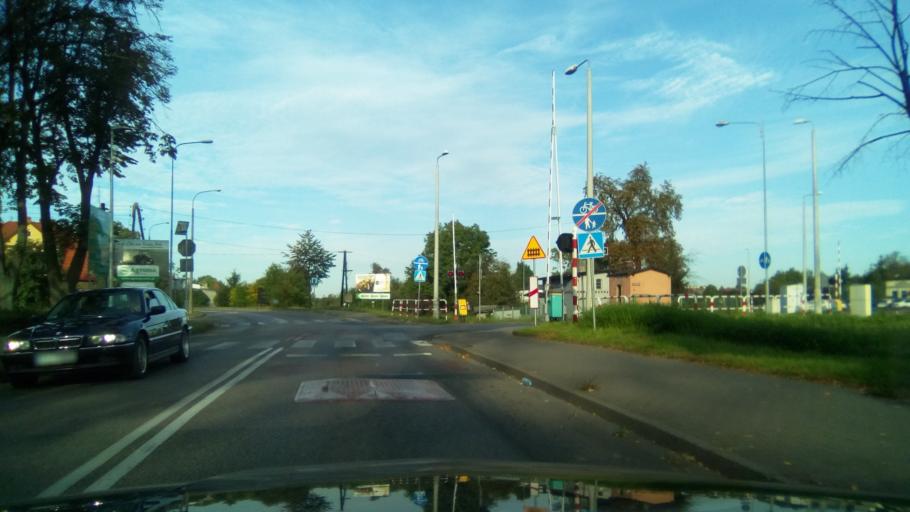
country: PL
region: Greater Poland Voivodeship
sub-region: Powiat wagrowiecki
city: Wagrowiec
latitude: 52.8080
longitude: 17.1894
